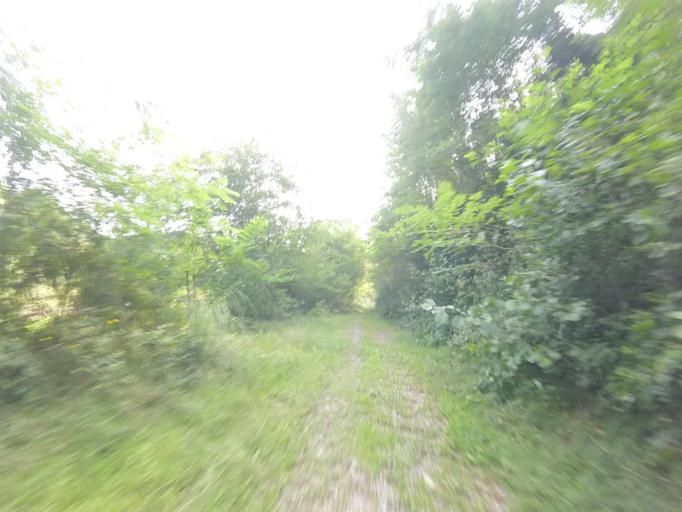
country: ES
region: Navarre
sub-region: Provincia de Navarra
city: Arano
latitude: 43.2290
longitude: -1.9332
